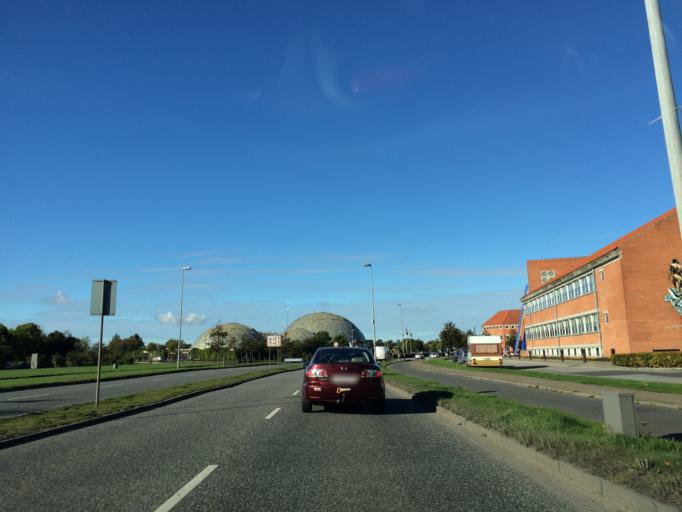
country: DK
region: Central Jutland
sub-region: Randers Kommune
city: Randers
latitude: 56.4569
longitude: 10.0370
